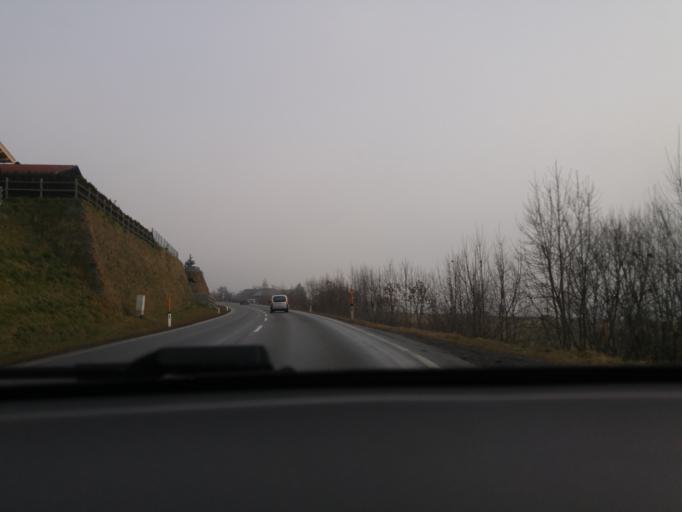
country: AT
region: Salzburg
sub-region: Politischer Bezirk Zell am See
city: Niedernsill
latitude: 47.2861
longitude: 12.6825
